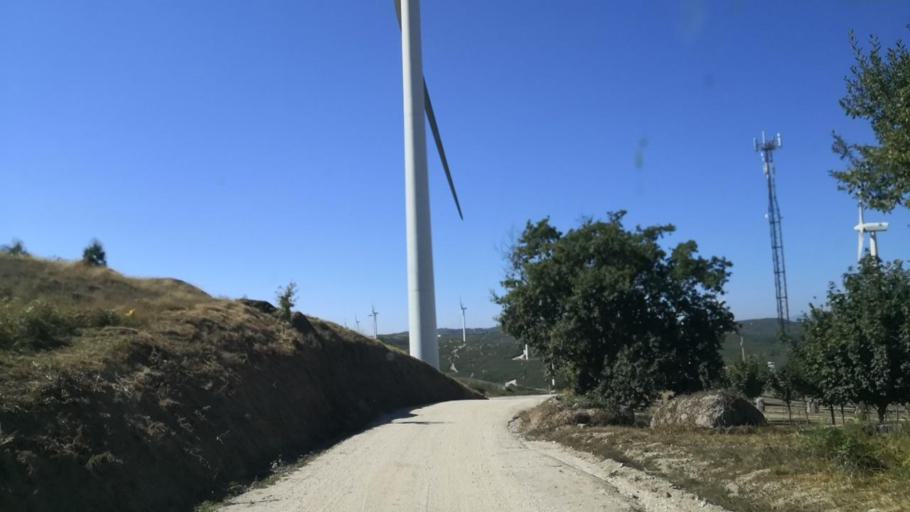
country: PT
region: Braga
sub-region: Cabeceiras de Basto
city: Refojos de Basto
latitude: 41.4920
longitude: -8.0715
